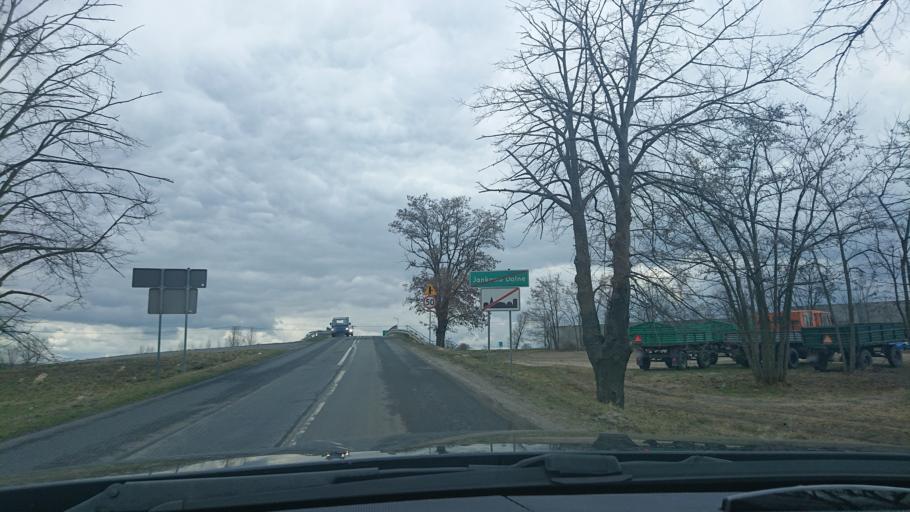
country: PL
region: Greater Poland Voivodeship
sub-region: Powiat gnieznienski
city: Niechanowo
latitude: 52.5535
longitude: 17.6981
